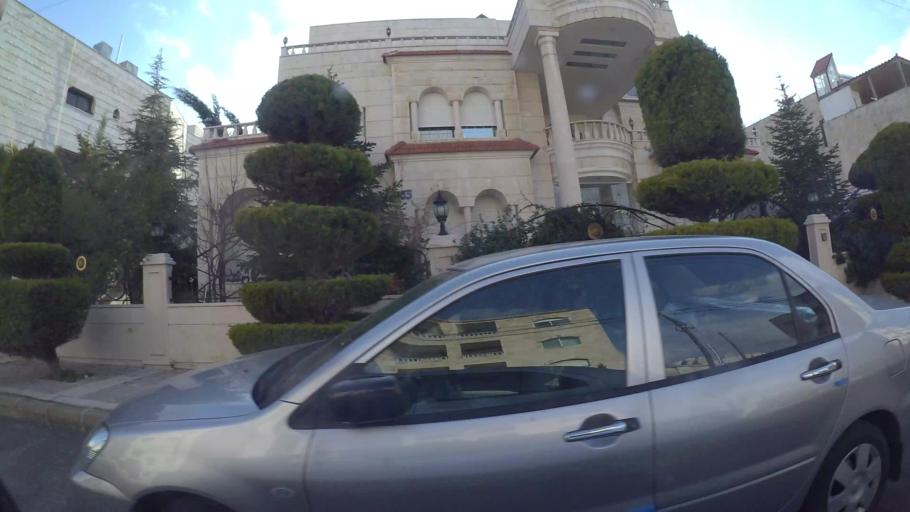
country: JO
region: Amman
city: Al Jubayhah
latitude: 32.0119
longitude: 35.8628
